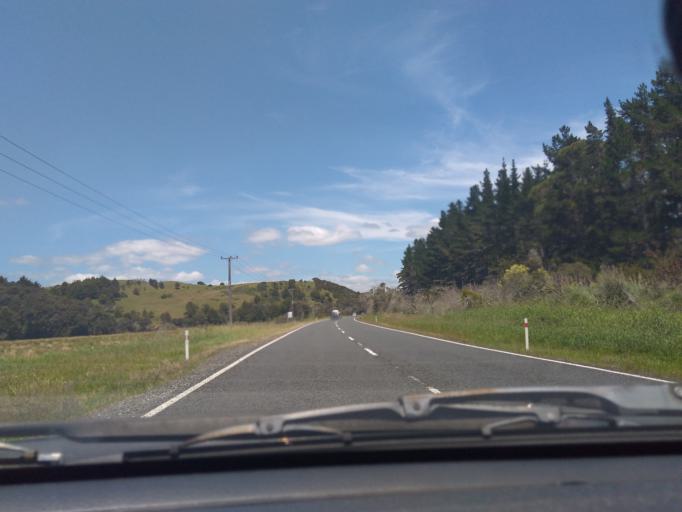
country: NZ
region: Northland
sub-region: Far North District
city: Taipa
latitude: -35.0543
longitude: 173.6862
